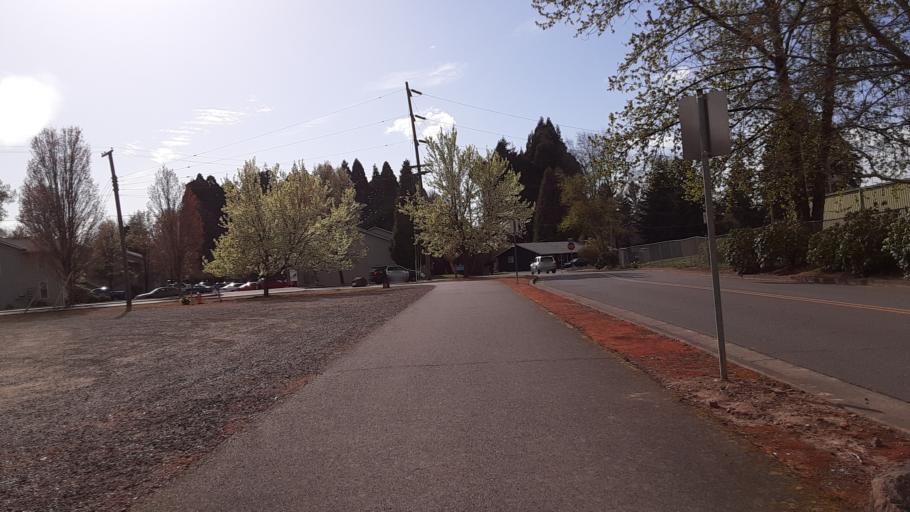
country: US
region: Oregon
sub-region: Benton County
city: Corvallis
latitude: 44.5506
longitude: -123.2559
